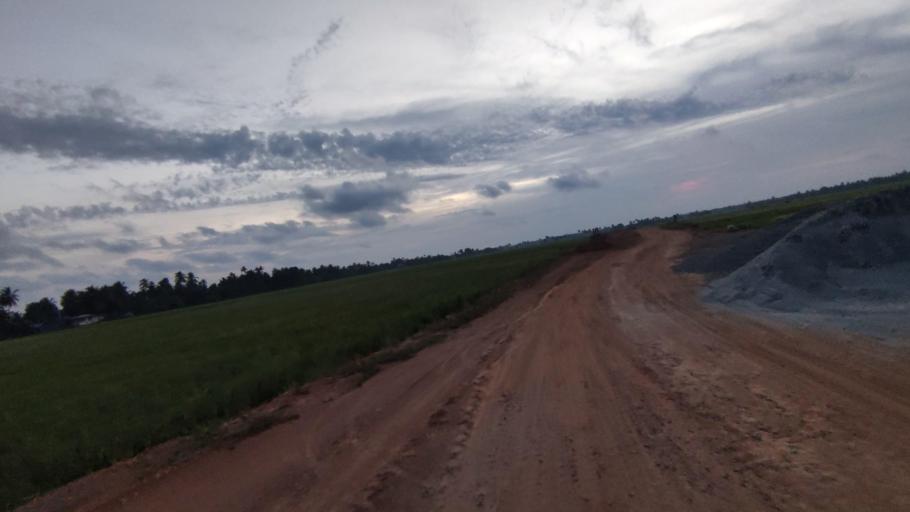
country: IN
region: Kerala
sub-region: Kottayam
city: Kottayam
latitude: 9.6436
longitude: 76.4497
